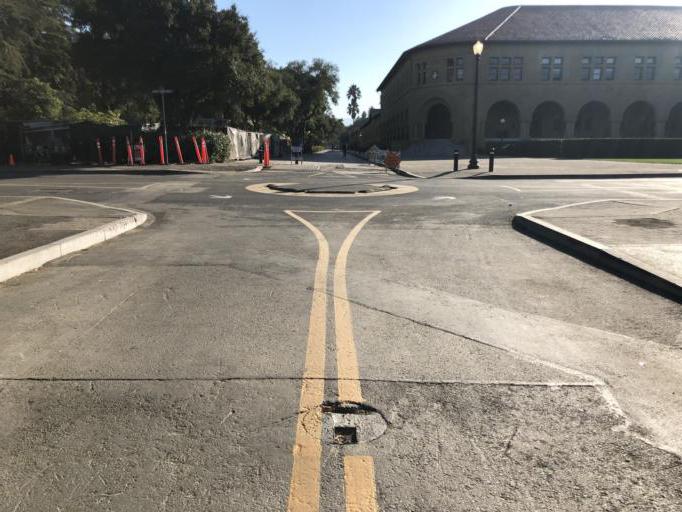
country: US
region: California
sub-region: Santa Clara County
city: Stanford
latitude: 37.4288
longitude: -122.1680
